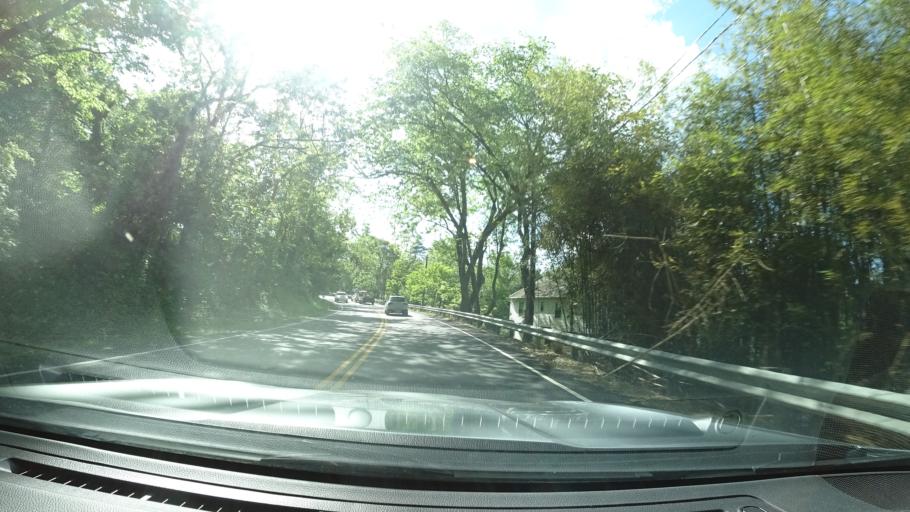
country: US
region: Virginia
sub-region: Fairfax County
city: McLean
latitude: 38.9243
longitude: -77.1585
